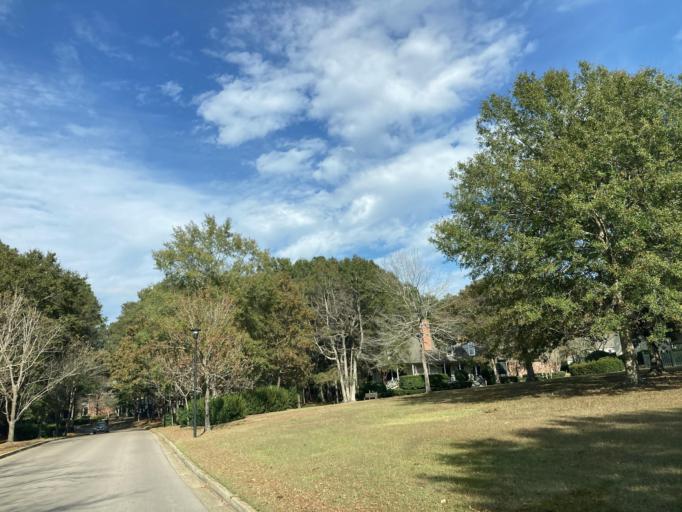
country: US
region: Mississippi
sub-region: Lamar County
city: West Hattiesburg
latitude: 31.3166
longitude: -89.4572
